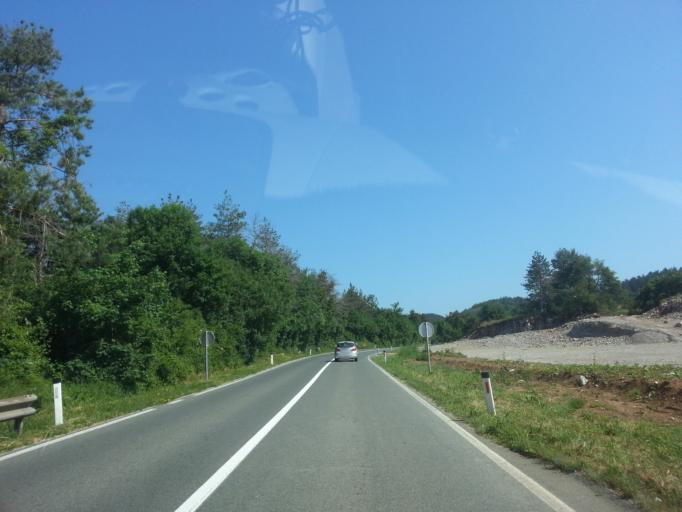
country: SI
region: Ilirska Bistrica
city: Ilirska Bistrica
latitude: 45.4944
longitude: 14.2736
